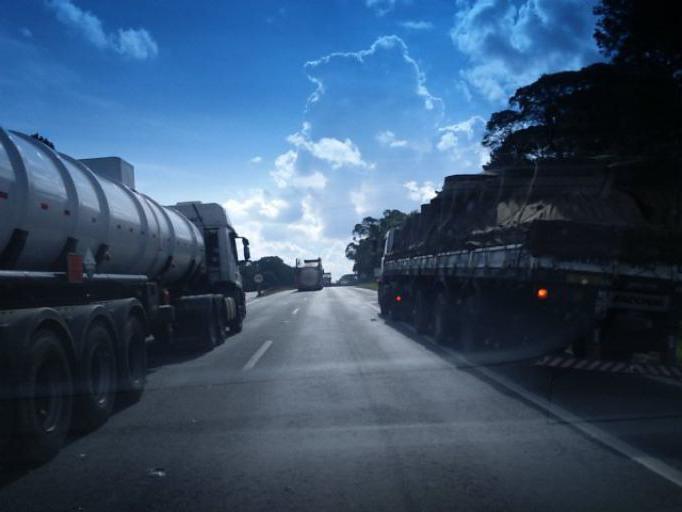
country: BR
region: Parana
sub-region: Campina Grande Do Sul
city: Campina Grande do Sul
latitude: -25.3070
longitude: -48.9777
